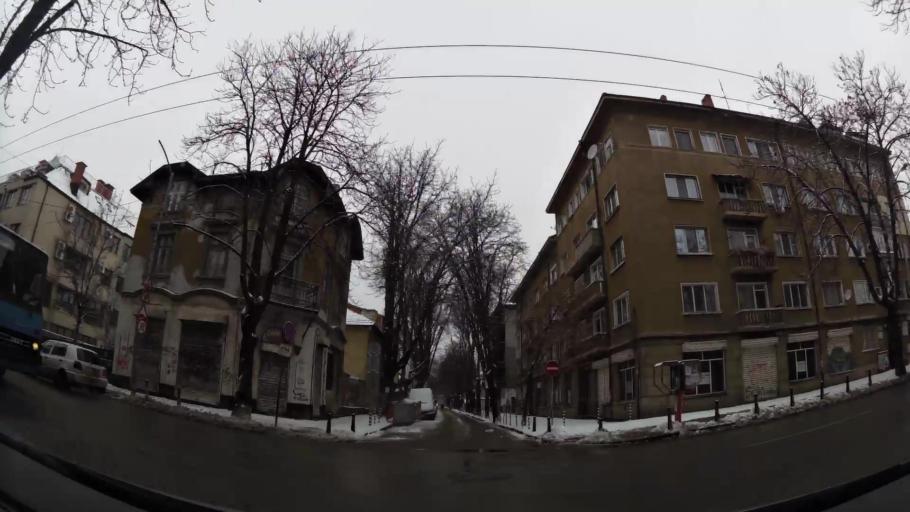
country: BG
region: Sofia-Capital
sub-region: Stolichna Obshtina
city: Sofia
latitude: 42.7062
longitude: 23.3286
